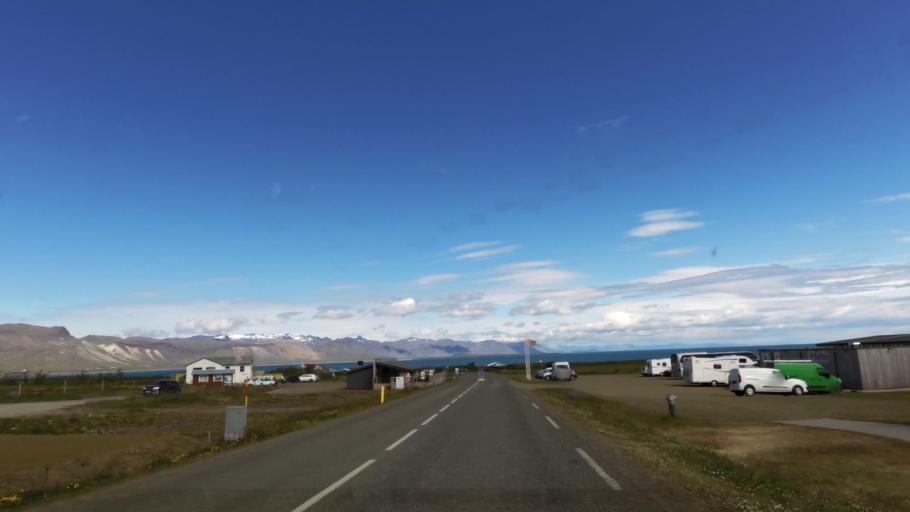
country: IS
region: West
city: Olafsvik
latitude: 64.7665
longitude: -23.6314
